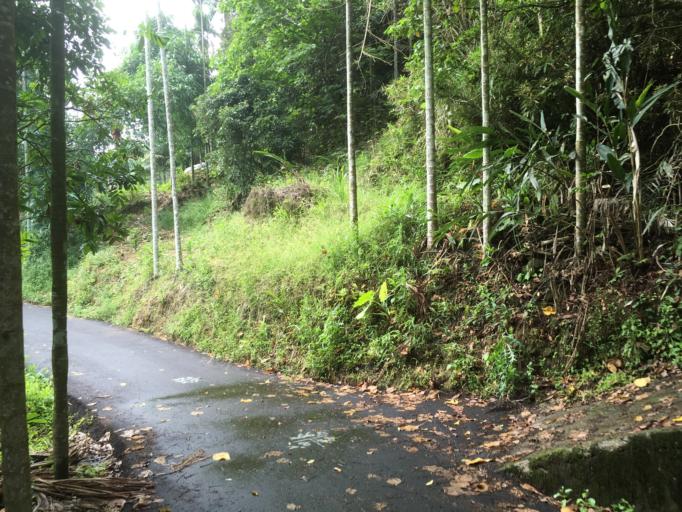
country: TW
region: Taiwan
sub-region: Taichung City
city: Taichung
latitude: 24.1705
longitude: 120.7781
